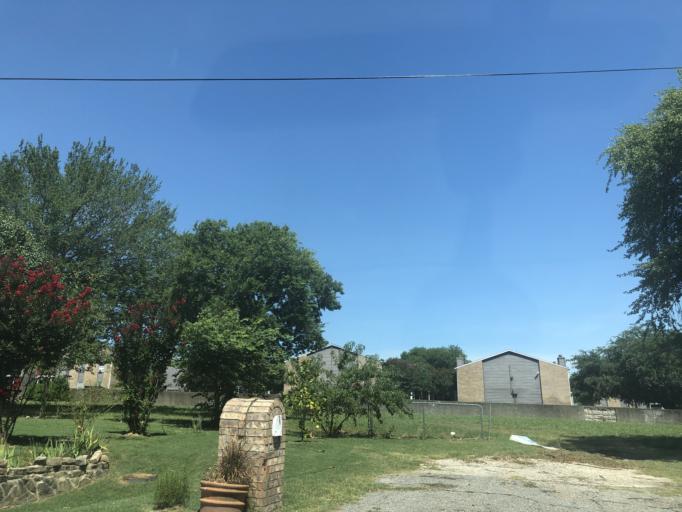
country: US
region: Texas
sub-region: Dallas County
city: Rowlett
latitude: 32.8506
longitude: -96.5966
